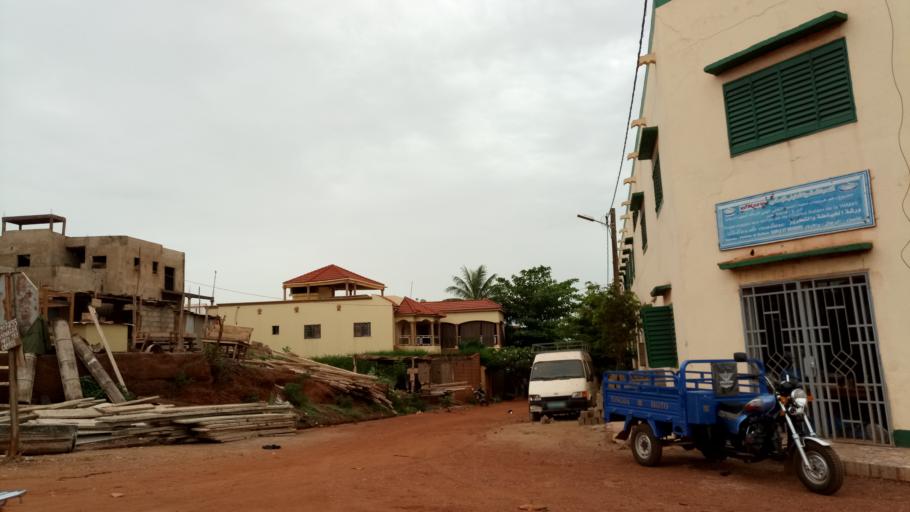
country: ML
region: Bamako
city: Bamako
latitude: 12.5840
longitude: -8.0114
